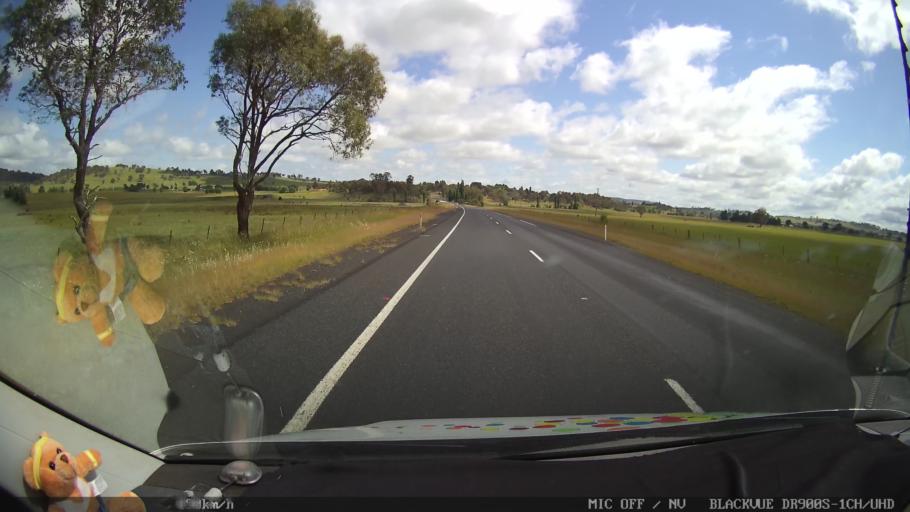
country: AU
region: New South Wales
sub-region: Glen Innes Severn
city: Glen Innes
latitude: -29.9390
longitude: 151.7232
